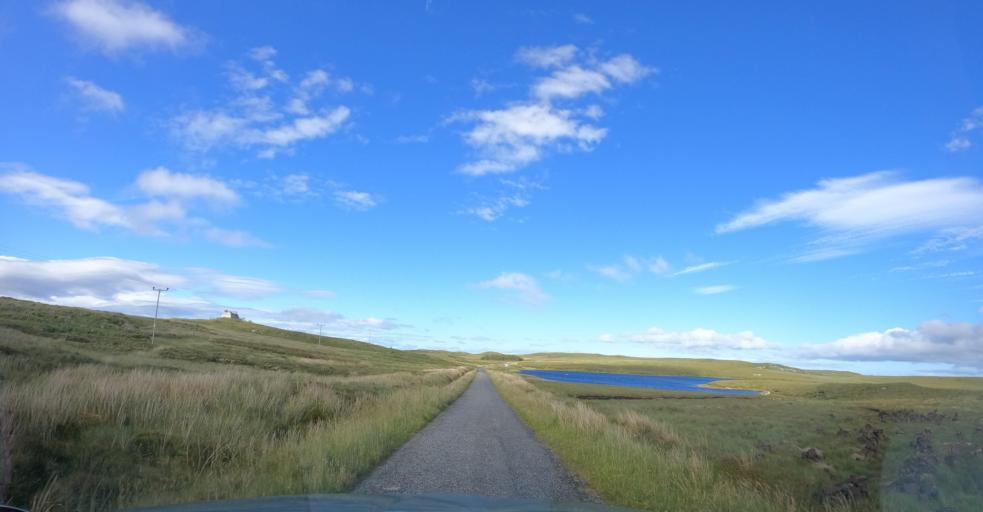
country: GB
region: Scotland
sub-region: Eilean Siar
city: Stornoway
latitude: 58.1771
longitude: -6.5532
